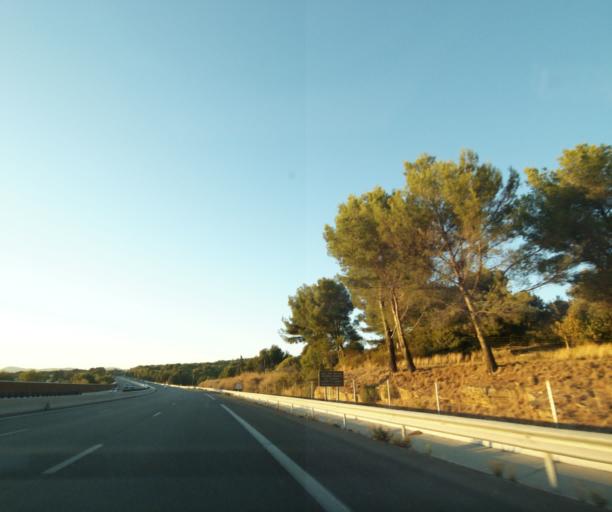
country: FR
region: Provence-Alpes-Cote d'Azur
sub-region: Departement des Bouches-du-Rhone
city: Ceyreste
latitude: 43.1943
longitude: 5.6500
